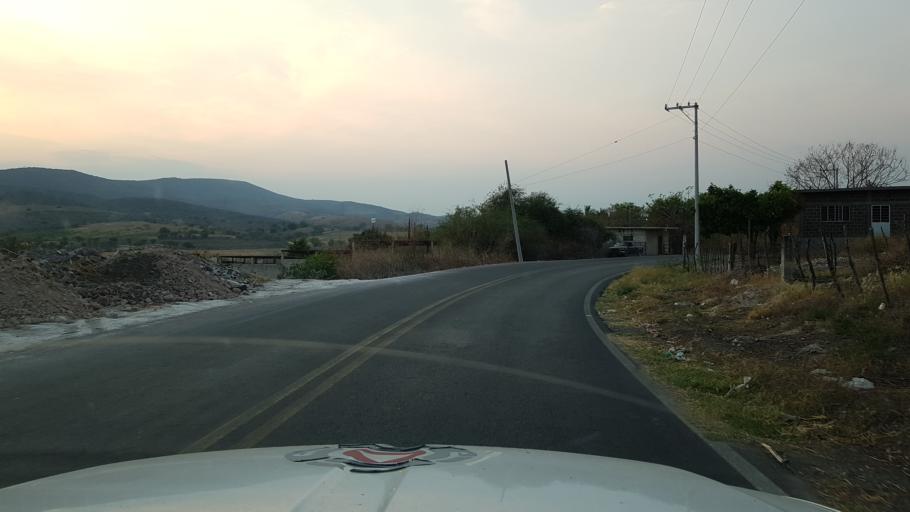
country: MX
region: Morelos
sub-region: Ayala
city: Abelardo L. Rodriguez
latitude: 18.7284
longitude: -99.0026
